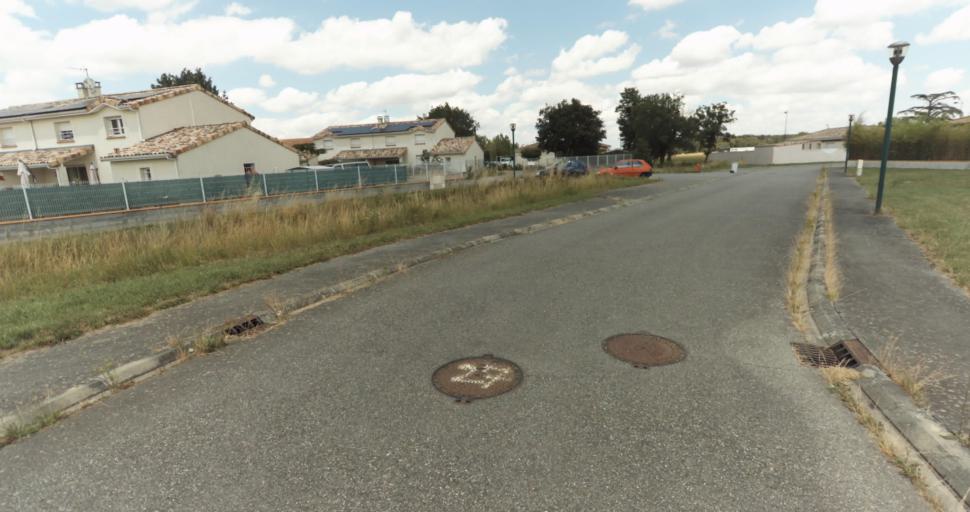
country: FR
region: Midi-Pyrenees
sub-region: Departement de la Haute-Garonne
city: Fontenilles
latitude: 43.5363
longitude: 1.1895
